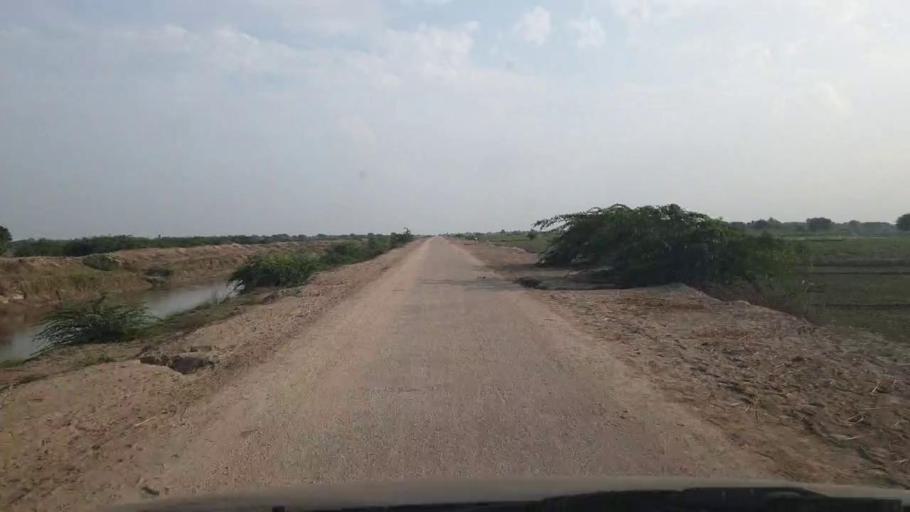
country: PK
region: Sindh
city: Badin
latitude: 24.5455
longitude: 68.6723
